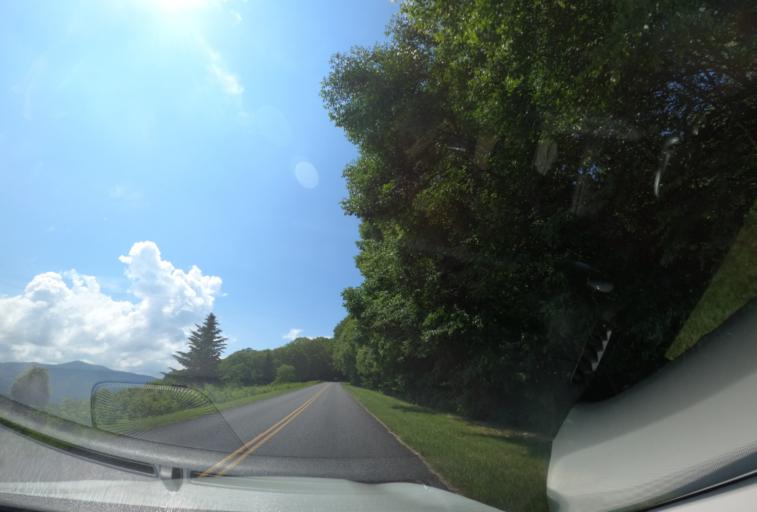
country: US
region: North Carolina
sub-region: Haywood County
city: Maggie Valley
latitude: 35.4513
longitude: -83.1043
